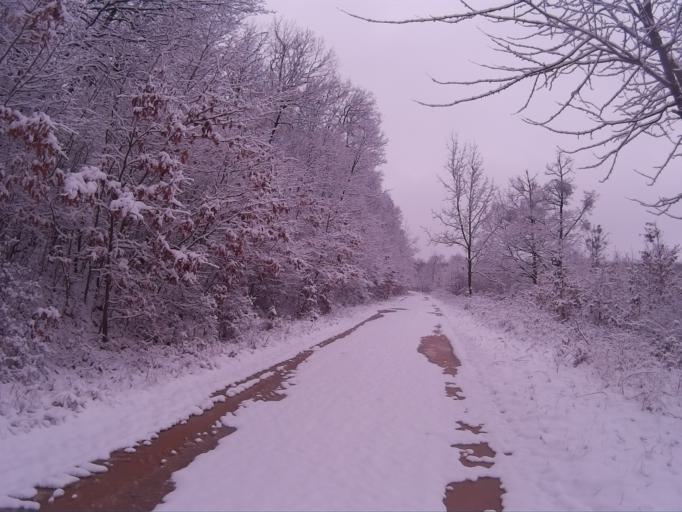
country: HU
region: Komarom-Esztergom
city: Tarjan
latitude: 47.5610
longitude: 18.5293
